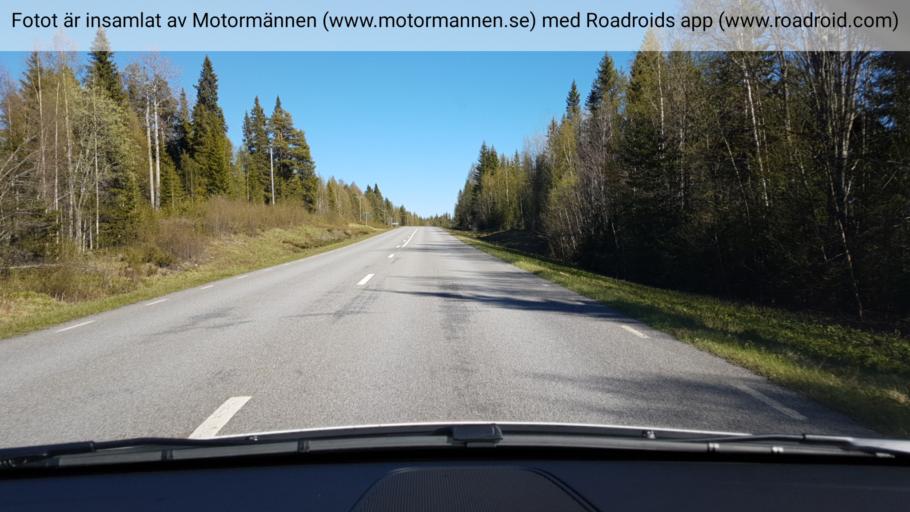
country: SE
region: Jaemtland
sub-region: Stroemsunds Kommun
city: Stroemsund
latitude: 64.3029
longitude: 15.3084
